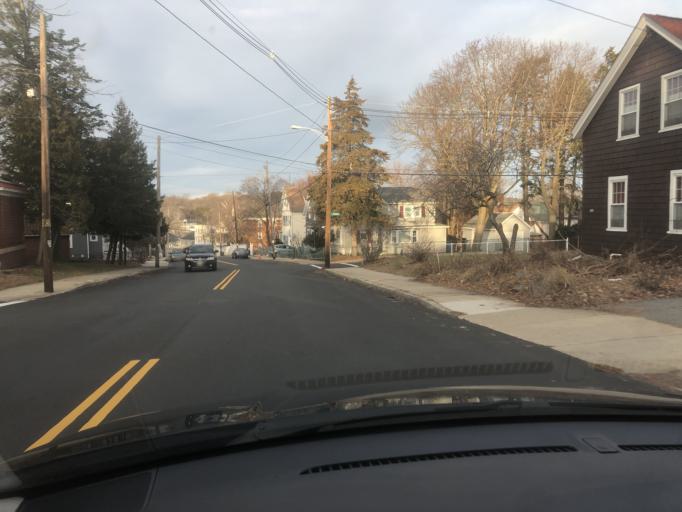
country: US
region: Massachusetts
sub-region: Essex County
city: Lawrence
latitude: 42.7215
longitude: -71.1539
